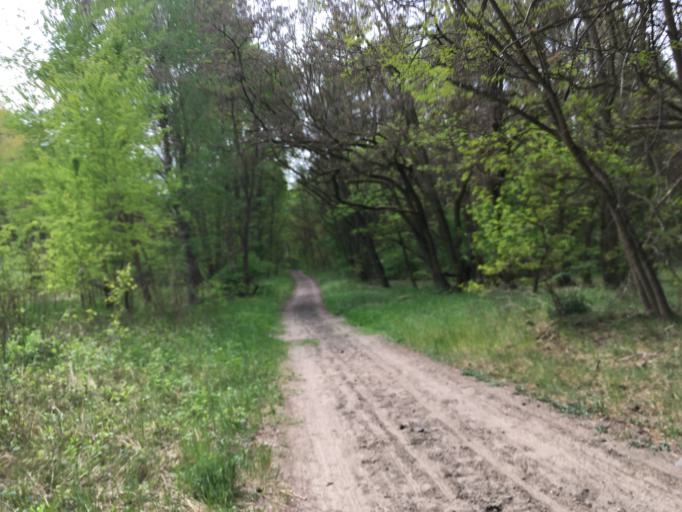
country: DE
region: Brandenburg
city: Rudnitz
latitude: 52.7041
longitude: 13.6215
